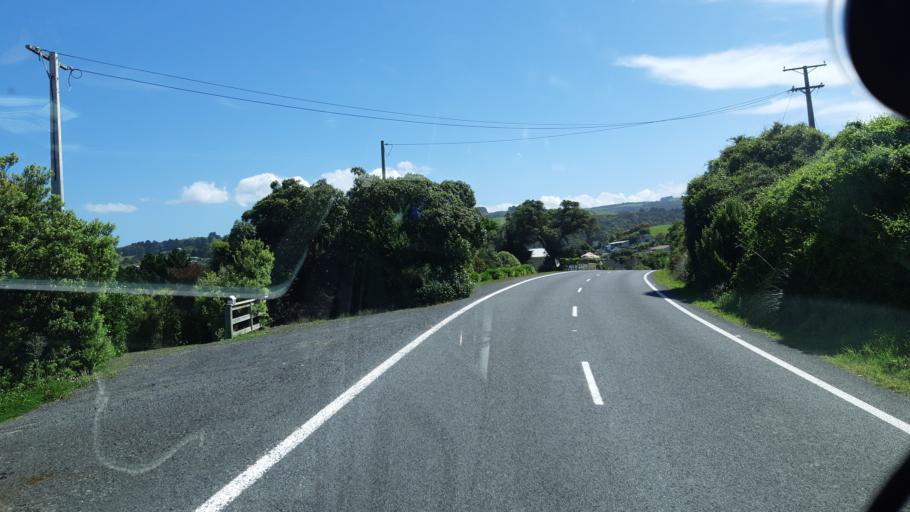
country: NZ
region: Otago
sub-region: Clutha District
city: Milton
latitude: -46.0514
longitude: 170.2033
